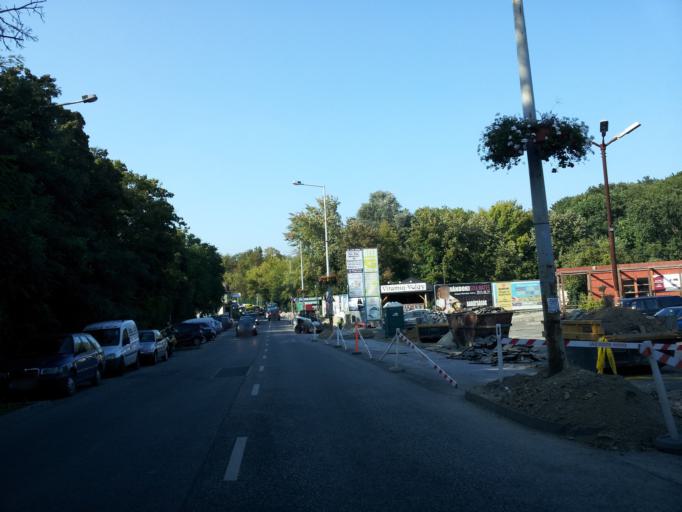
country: HU
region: Pest
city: Budakeszi
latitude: 47.5413
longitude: 18.9653
